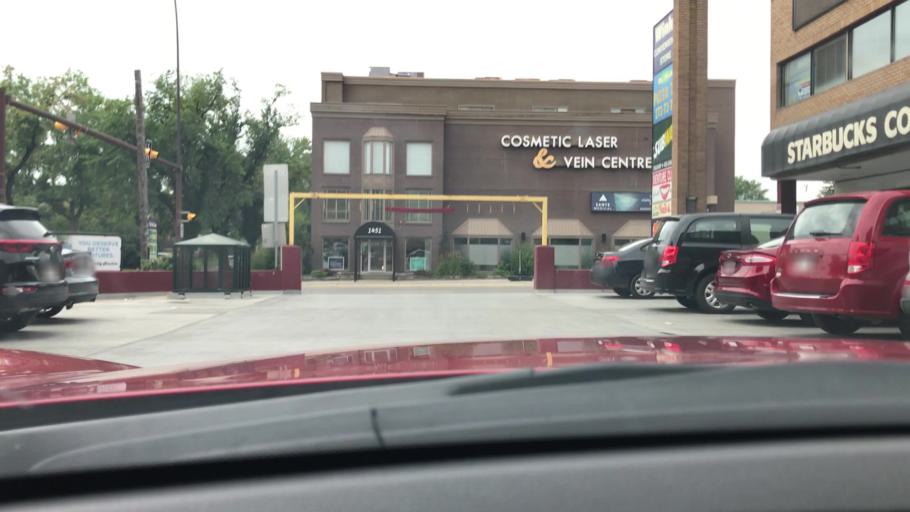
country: CA
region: Alberta
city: Calgary
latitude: 51.0396
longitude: -114.0942
